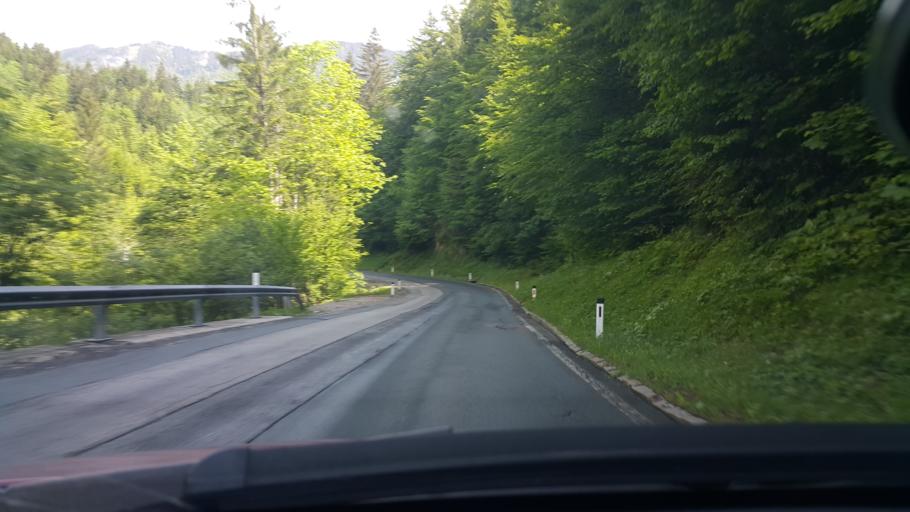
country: AT
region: Carinthia
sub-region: Politischer Bezirk Klagenfurt Land
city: Ferlach
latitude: 46.4688
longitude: 14.2583
